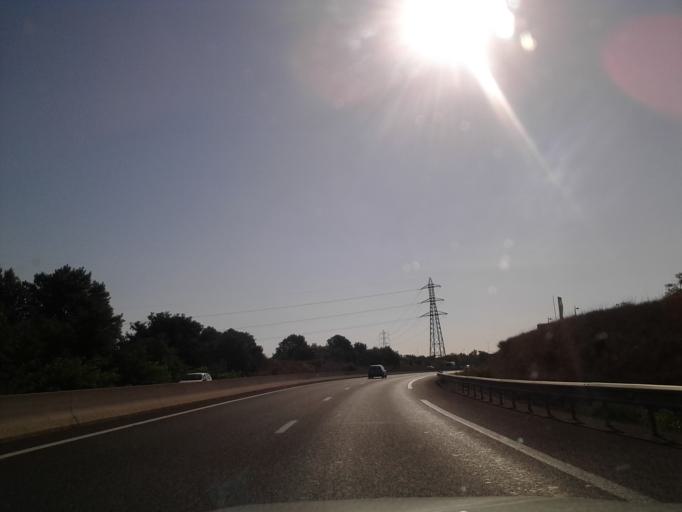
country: FR
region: Languedoc-Roussillon
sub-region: Departement des Pyrenees-Orientales
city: Saint-Esteve
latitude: 42.6944
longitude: 2.8446
